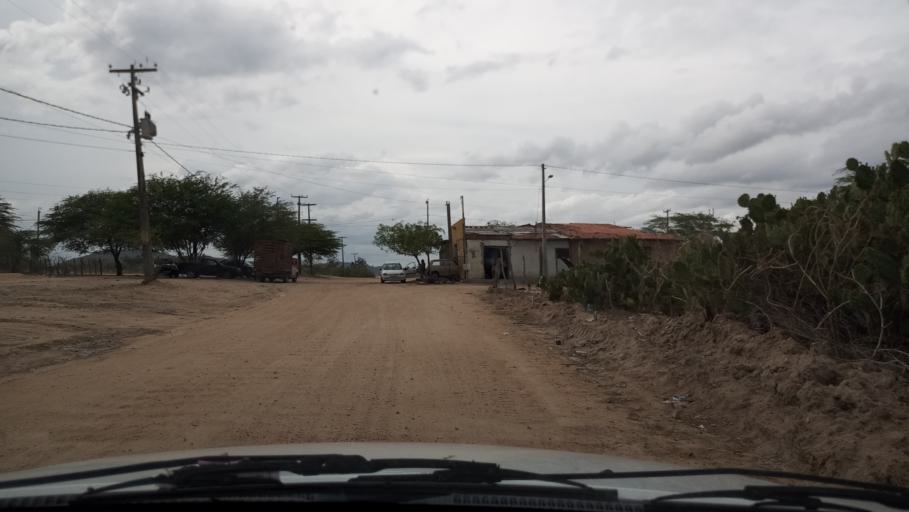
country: BR
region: Rio Grande do Norte
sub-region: Tangara
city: Tangara
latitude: -6.1901
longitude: -35.8015
